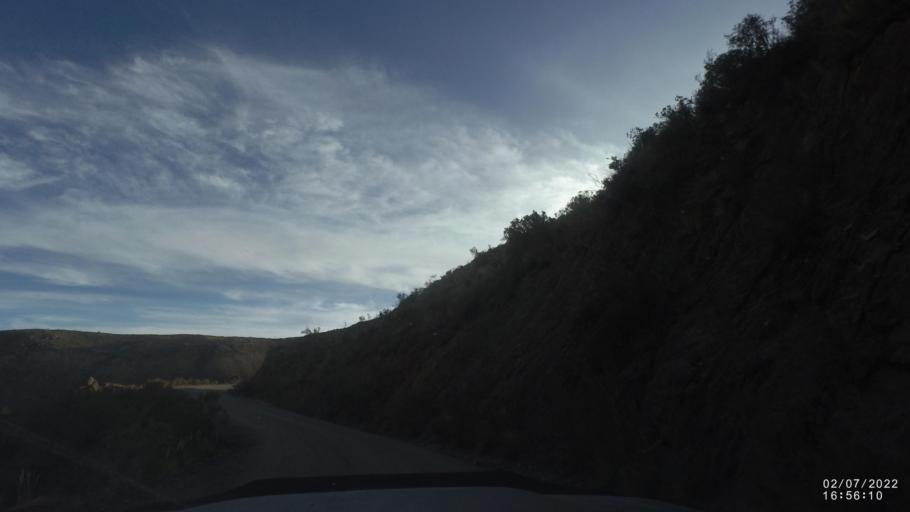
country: BO
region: Cochabamba
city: Irpa Irpa
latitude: -17.9561
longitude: -66.5430
